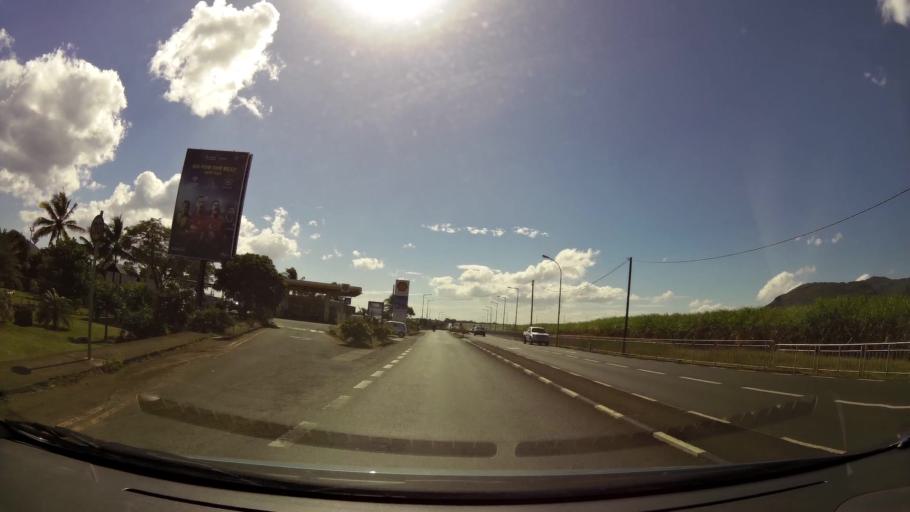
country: MU
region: Black River
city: Cascavelle
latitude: -20.2797
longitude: 57.4044
